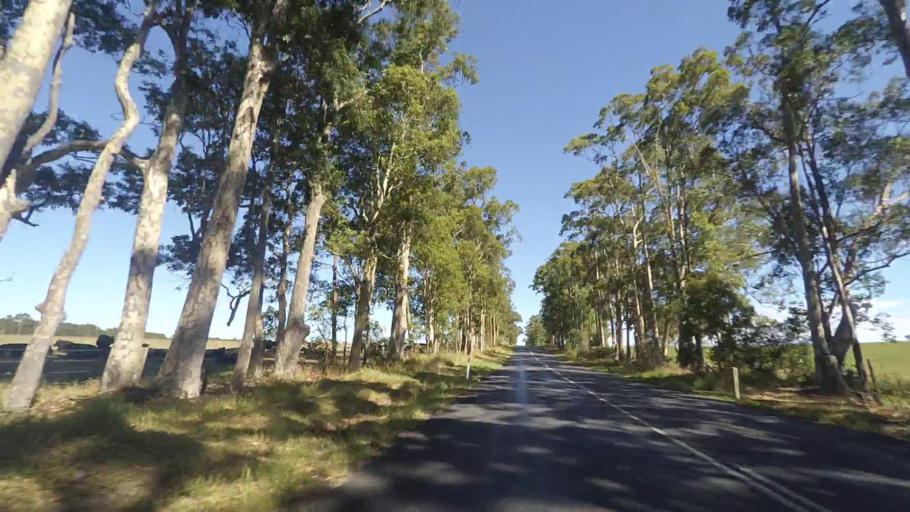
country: AU
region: New South Wales
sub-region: Great Lakes
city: Hawks Nest
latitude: -32.6246
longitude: 152.1295
